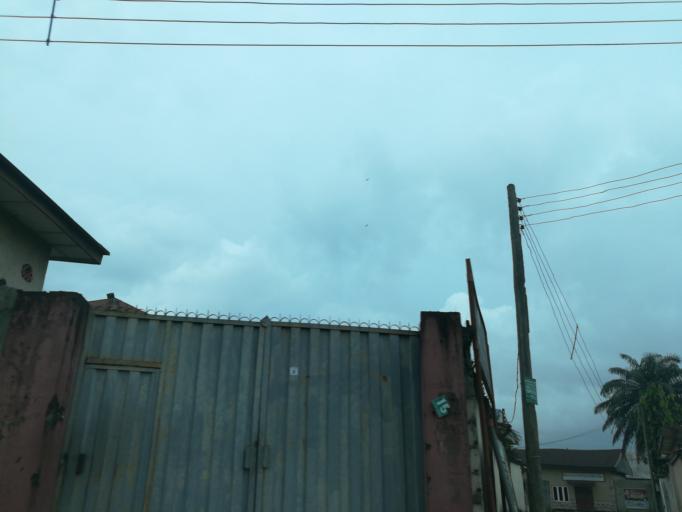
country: NG
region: Rivers
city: Port Harcourt
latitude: 4.8157
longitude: 7.0158
